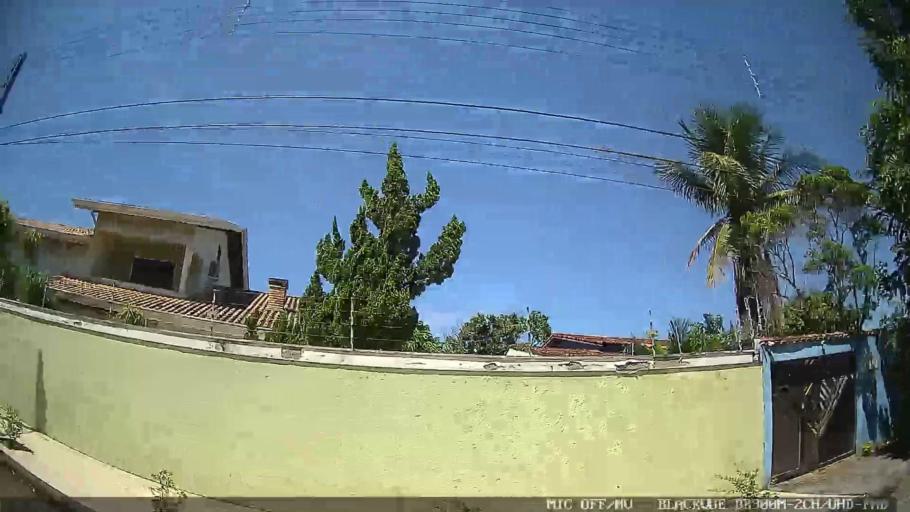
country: BR
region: Sao Paulo
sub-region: Peruibe
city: Peruibe
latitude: -24.3018
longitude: -46.9766
